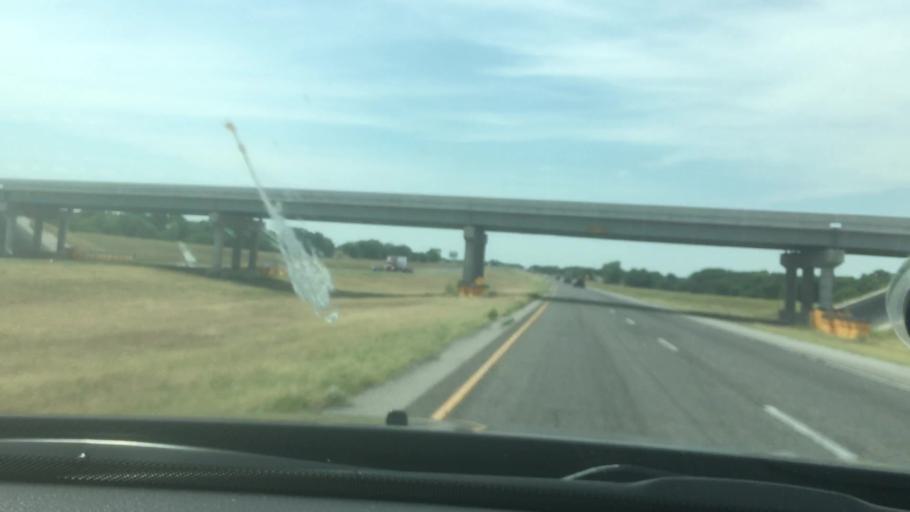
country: US
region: Oklahoma
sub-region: Garvin County
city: Wynnewood
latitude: 34.5726
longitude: -97.1996
